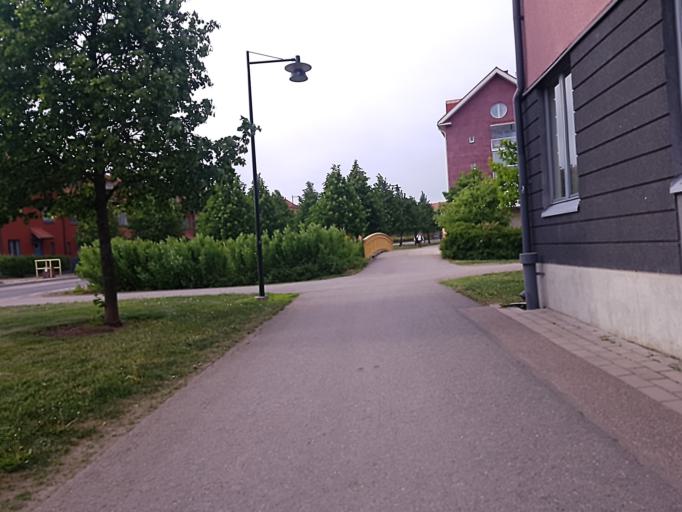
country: FI
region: Uusimaa
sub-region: Helsinki
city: Vantaa
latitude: 60.2830
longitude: 24.9591
